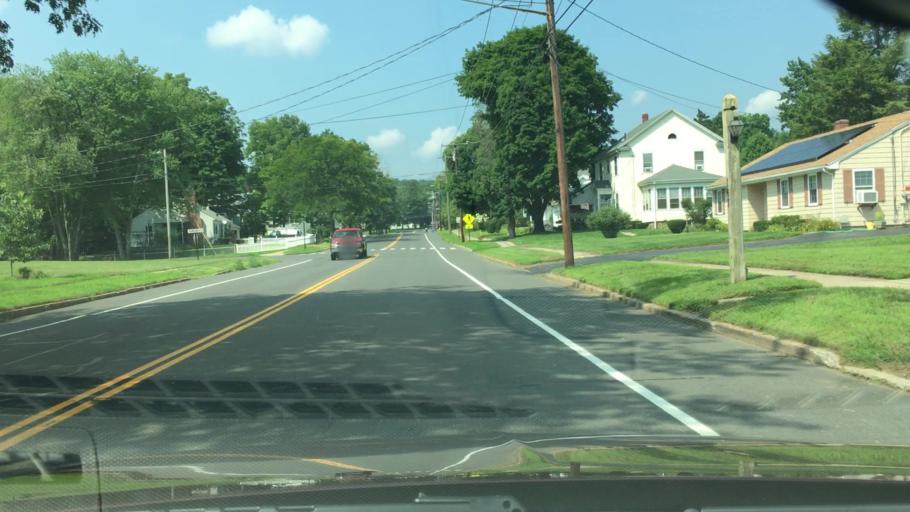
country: US
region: Connecticut
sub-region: Hartford County
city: Plainville
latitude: 41.6667
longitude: -72.8780
